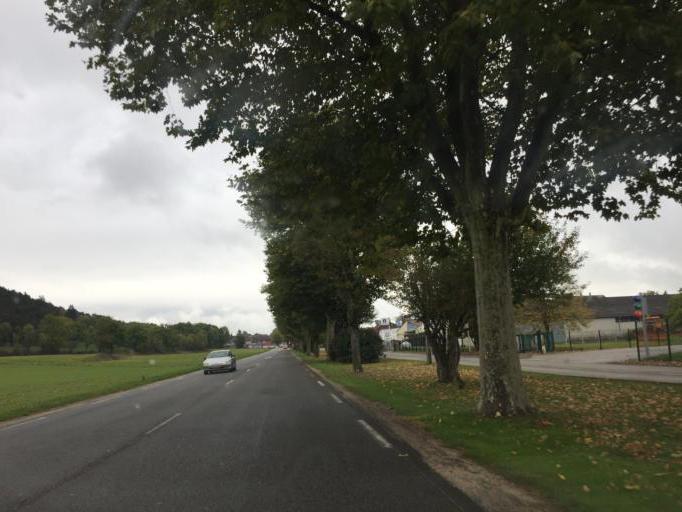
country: FR
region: Franche-Comte
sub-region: Departement du Jura
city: Orgelet
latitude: 46.5303
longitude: 5.6063
